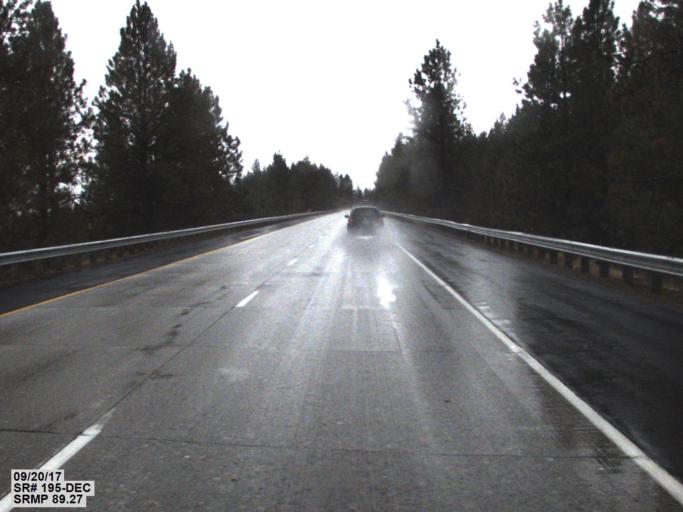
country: US
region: Washington
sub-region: Spokane County
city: Spokane
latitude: 47.5612
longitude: -117.3967
